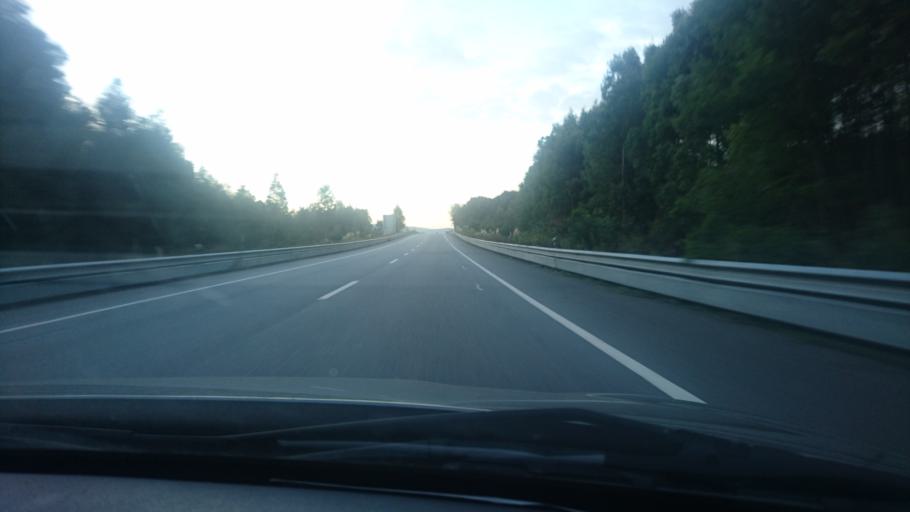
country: PT
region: Aveiro
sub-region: Santa Maria da Feira
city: Arrifana
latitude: 40.9187
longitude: -8.4897
